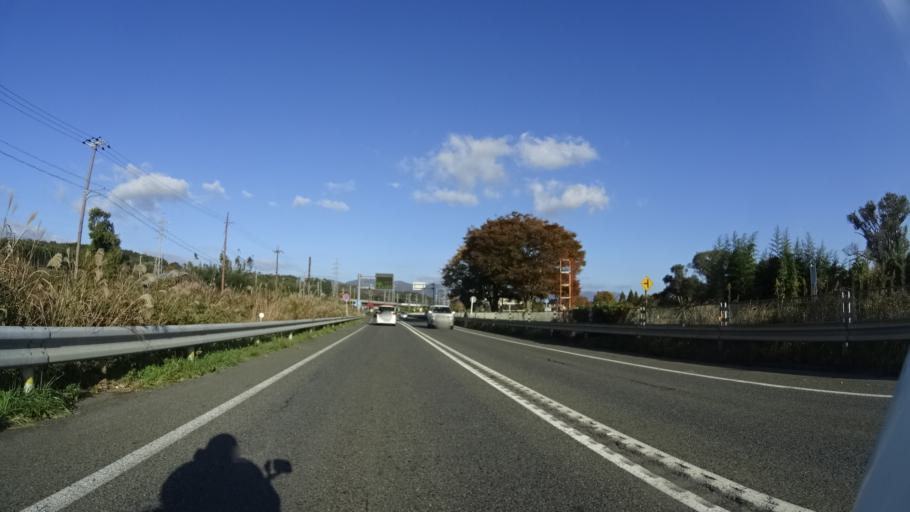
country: JP
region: Shiga Prefecture
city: Nagahama
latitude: 35.3781
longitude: 136.0355
